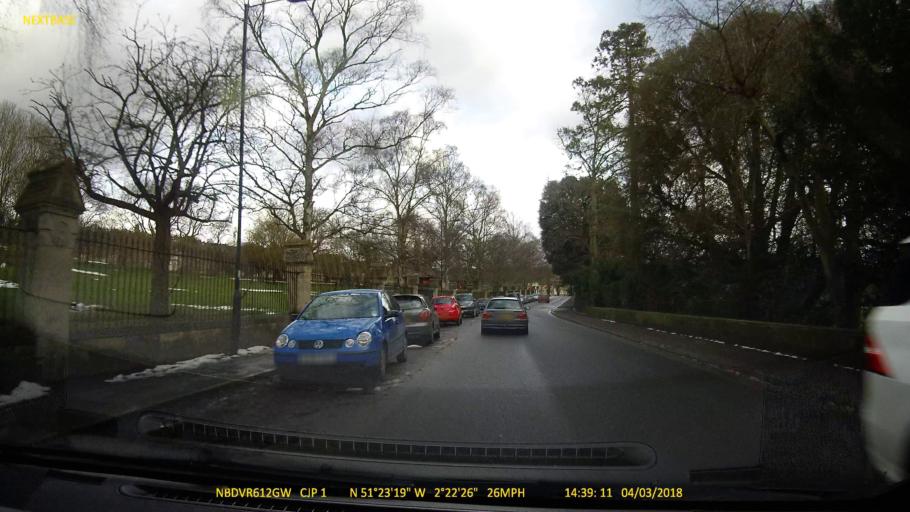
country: GB
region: England
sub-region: Bath and North East Somerset
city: Bath
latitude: 51.3888
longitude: -2.3738
